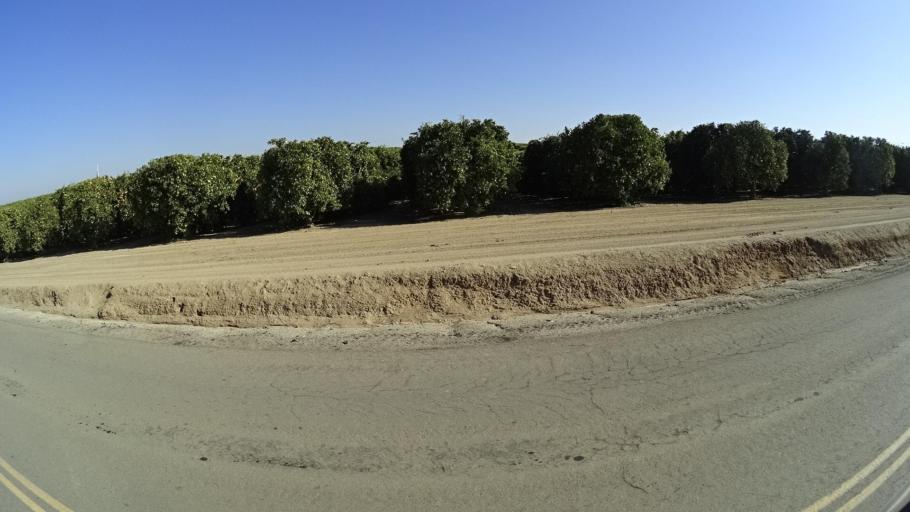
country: US
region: California
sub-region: Tulare County
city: Richgrove
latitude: 35.7124
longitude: -119.1339
